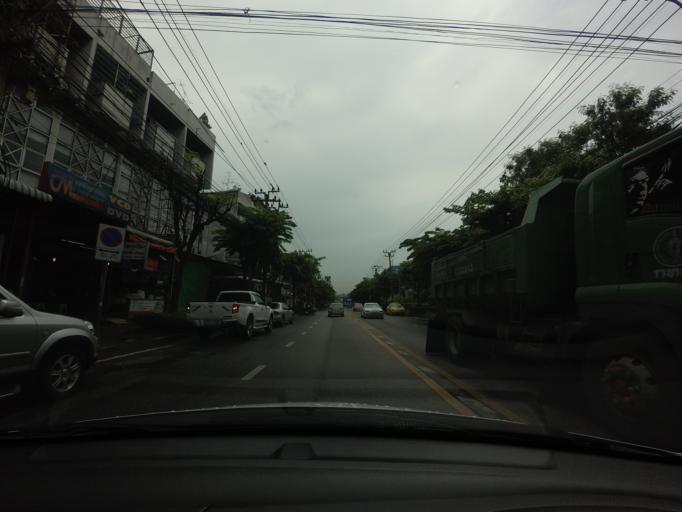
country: TH
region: Bangkok
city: Phra Khanong
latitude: 13.7097
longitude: 100.6255
